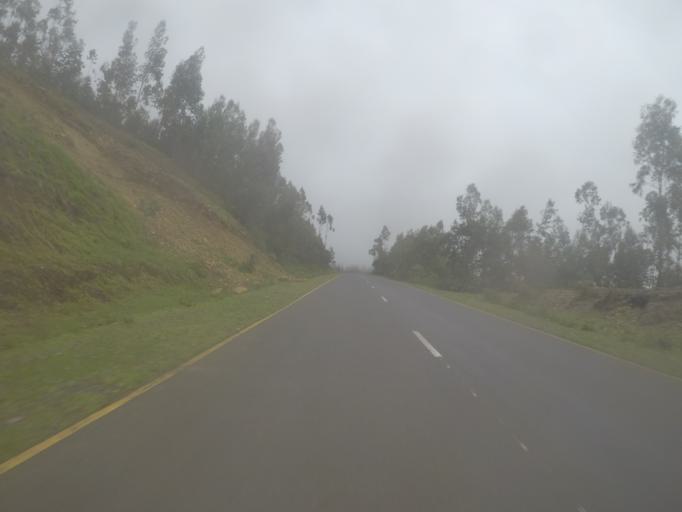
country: ET
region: Amhara
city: Gondar
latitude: 12.7499
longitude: 37.5332
